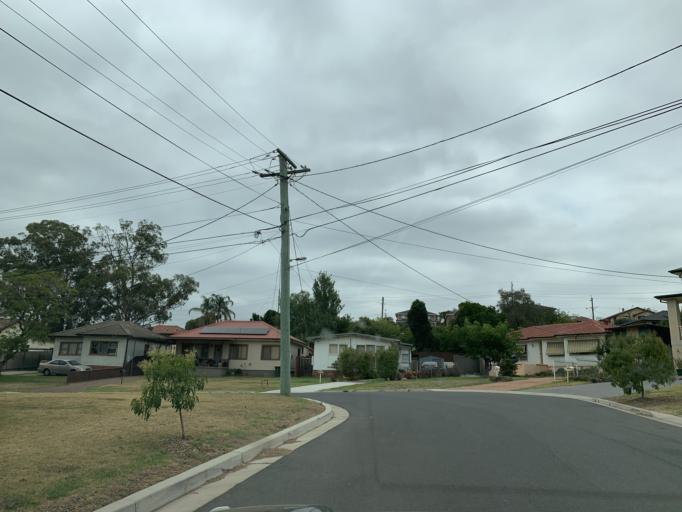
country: AU
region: New South Wales
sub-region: Blacktown
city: Blacktown
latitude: -33.7743
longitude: 150.8937
